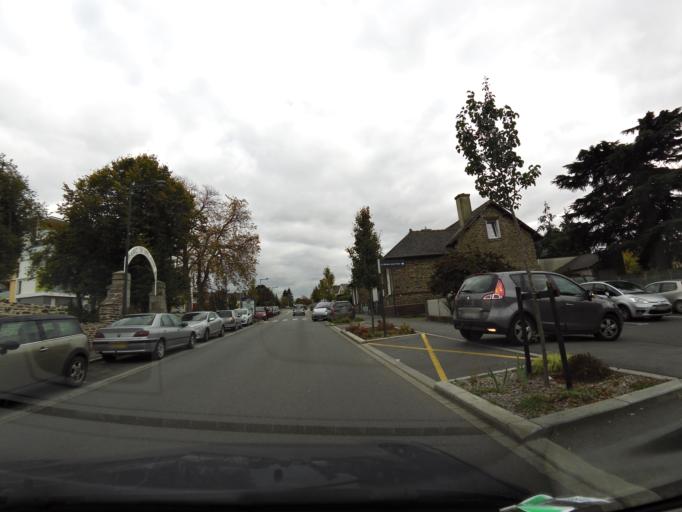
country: FR
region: Brittany
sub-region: Departement d'Ille-et-Vilaine
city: Chantepie
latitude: 48.0870
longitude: -1.6162
